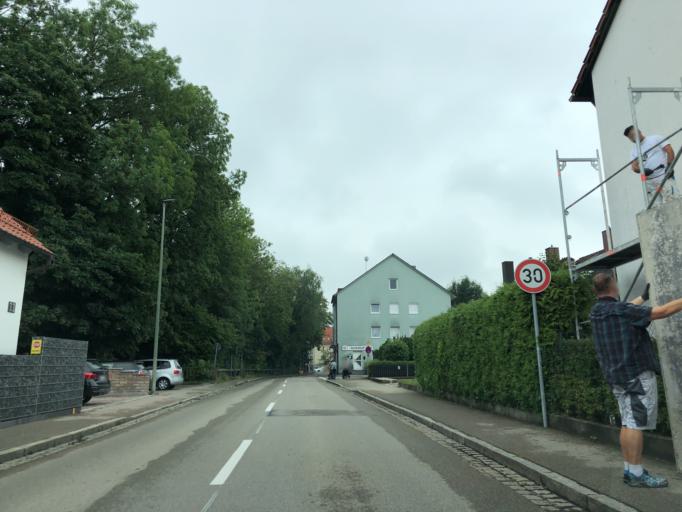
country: DE
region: Bavaria
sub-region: Upper Bavaria
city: Erding
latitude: 48.3071
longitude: 11.9051
